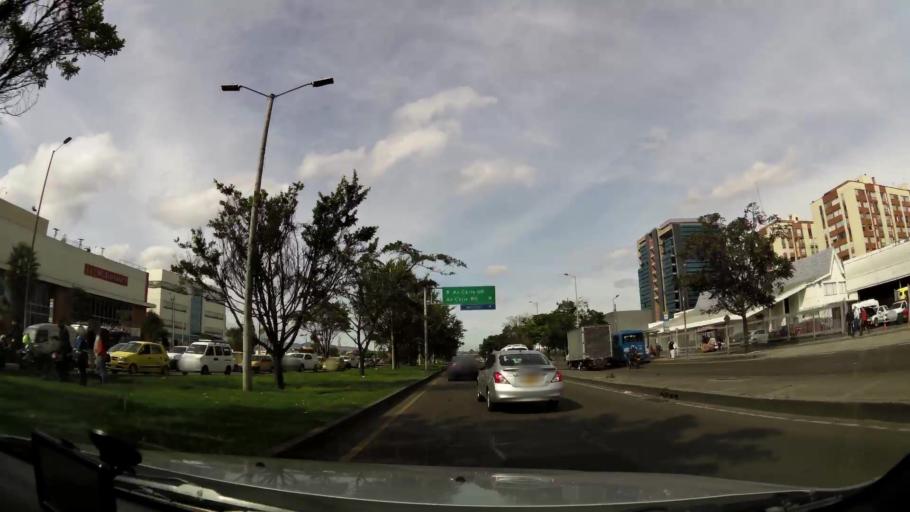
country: CO
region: Bogota D.C.
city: Barrio San Luis
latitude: 4.6872
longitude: -74.0750
